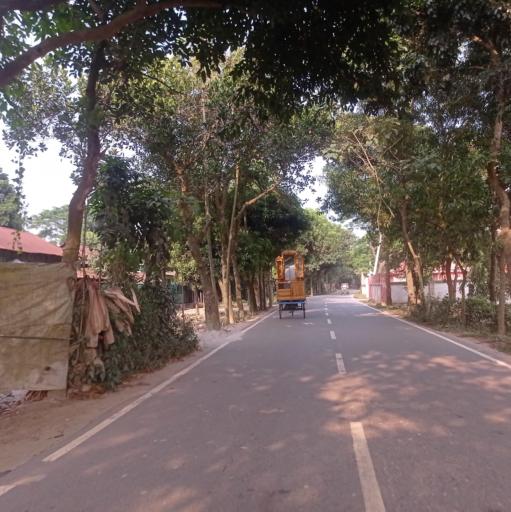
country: BD
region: Dhaka
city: Bhairab Bazar
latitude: 24.0936
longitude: 90.8513
